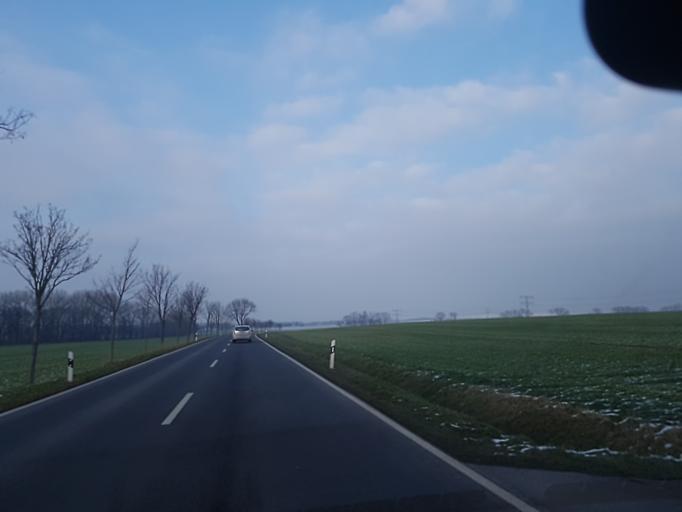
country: DE
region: Saxony
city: Oschatz
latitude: 51.3262
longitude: 13.0911
